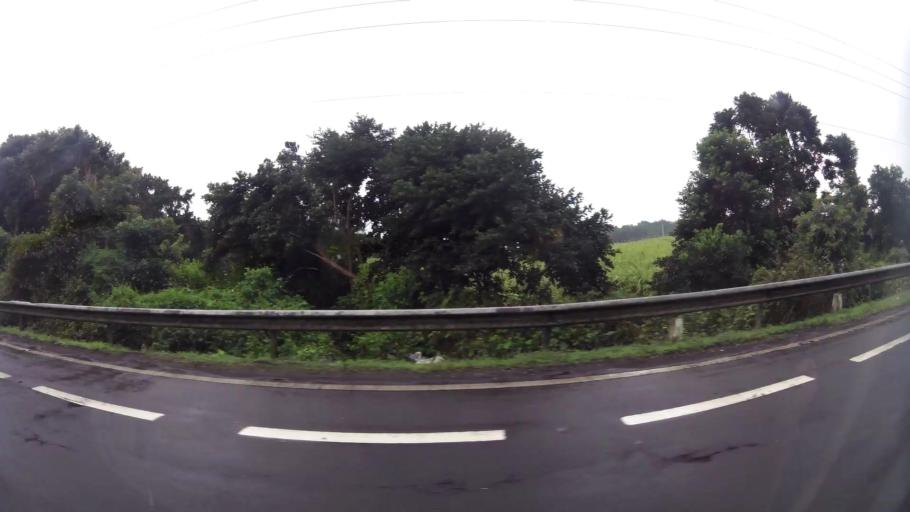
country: MU
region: Plaines Wilhems
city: Curepipe
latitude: -20.3045
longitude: 57.5380
